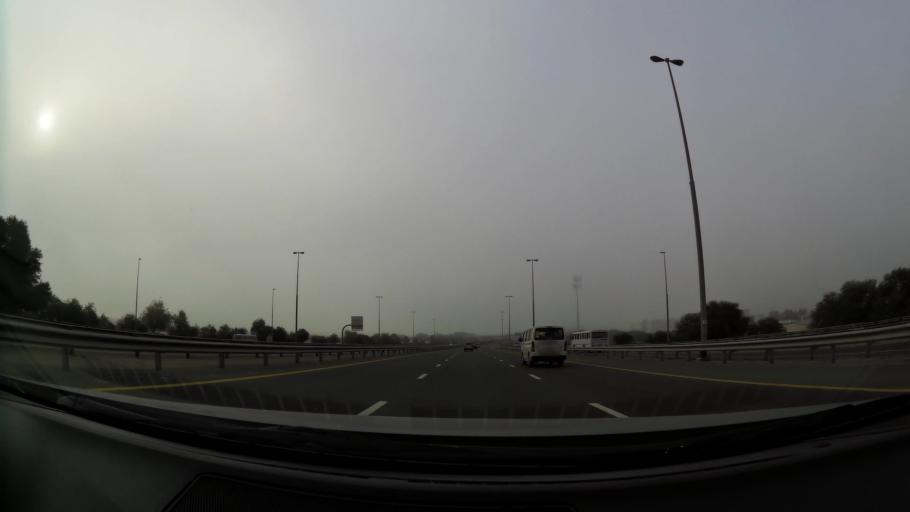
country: AE
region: Ash Shariqah
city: Sharjah
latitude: 25.1794
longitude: 55.3168
